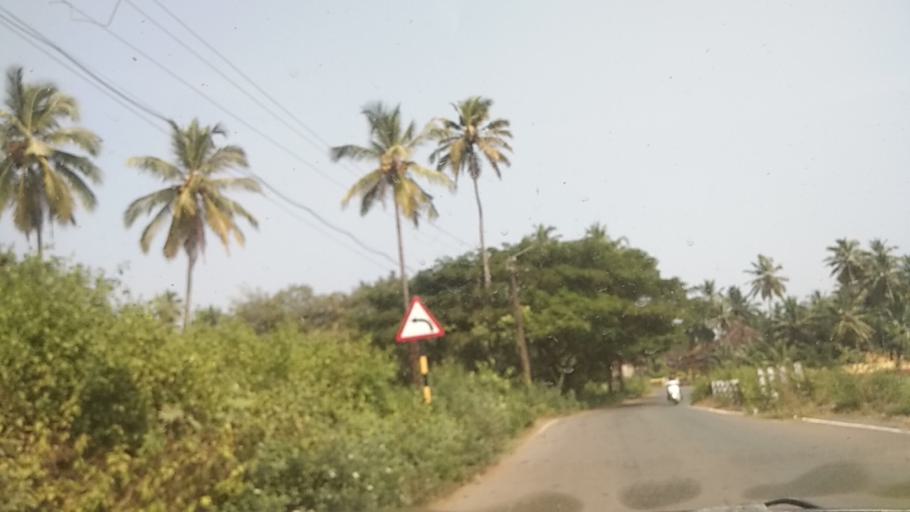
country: IN
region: Goa
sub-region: South Goa
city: Cavelossim
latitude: 15.1620
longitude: 73.9664
